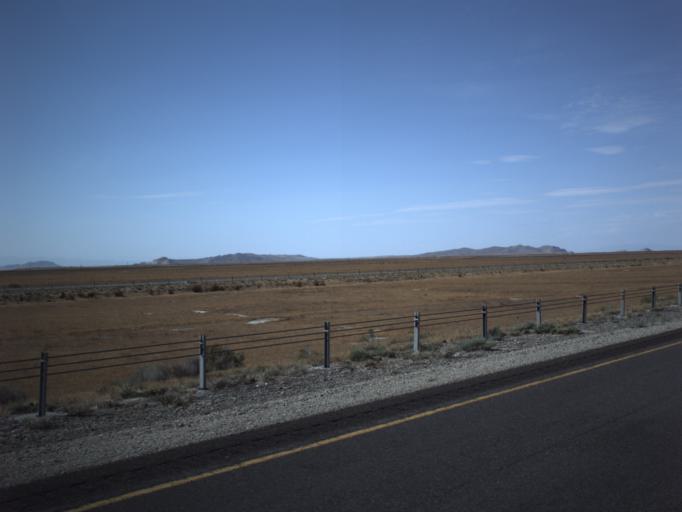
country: US
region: Utah
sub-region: Tooele County
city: Grantsville
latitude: 40.7260
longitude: -113.1495
